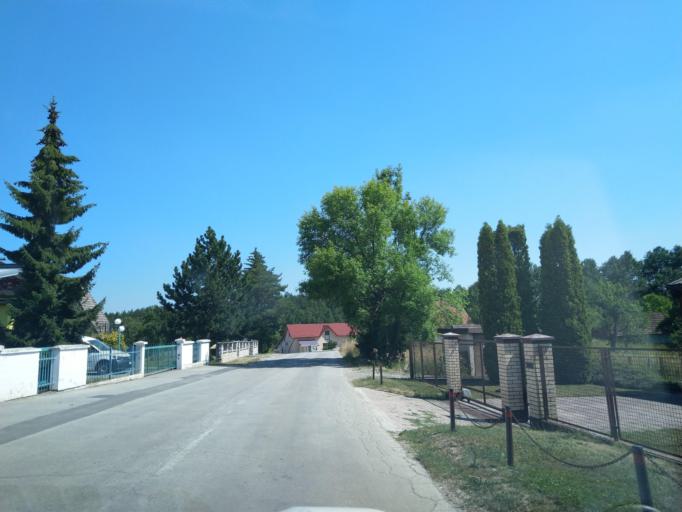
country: RS
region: Central Serbia
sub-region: Zlatiborski Okrug
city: Uzice
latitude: 43.8051
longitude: 19.8129
